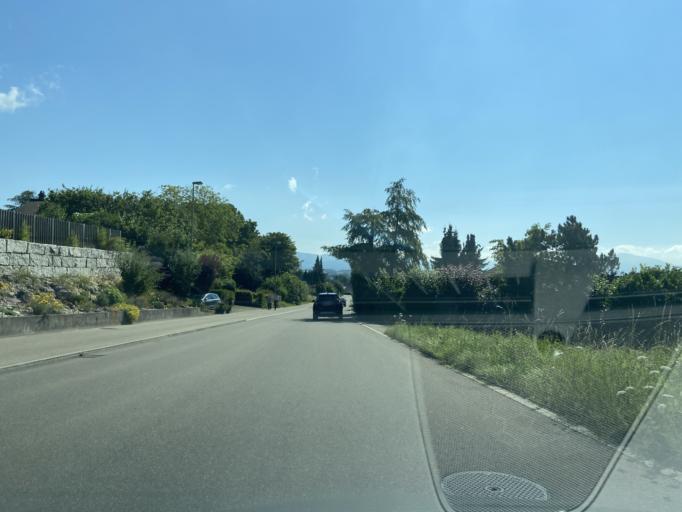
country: CH
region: Zurich
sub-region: Bezirk Meilen
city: Uerikon
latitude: 47.2491
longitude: 8.7553
